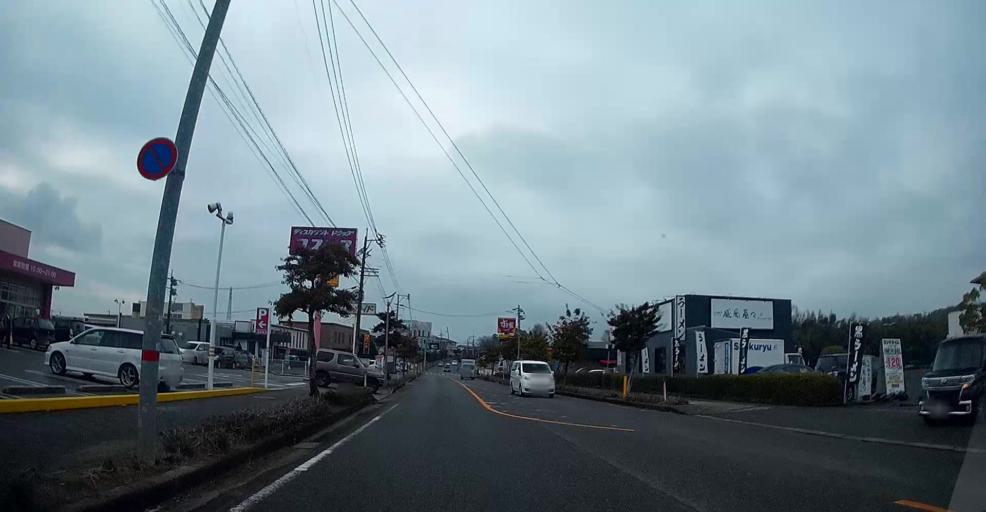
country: JP
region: Kumamoto
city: Matsubase
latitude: 32.6570
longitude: 130.6883
